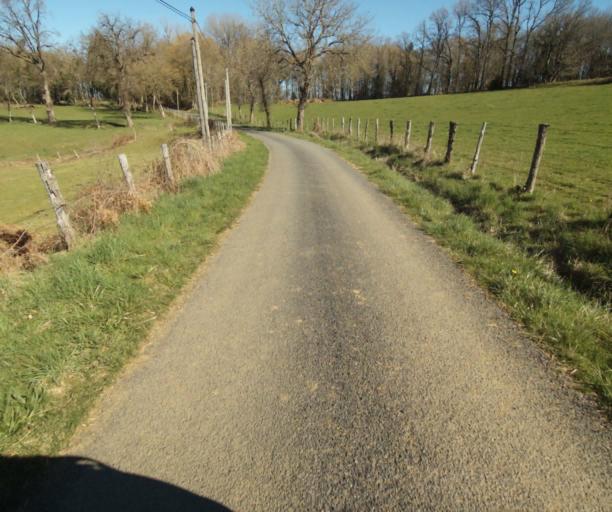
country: FR
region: Limousin
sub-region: Departement de la Correze
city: Chamboulive
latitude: 45.4091
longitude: 1.6877
